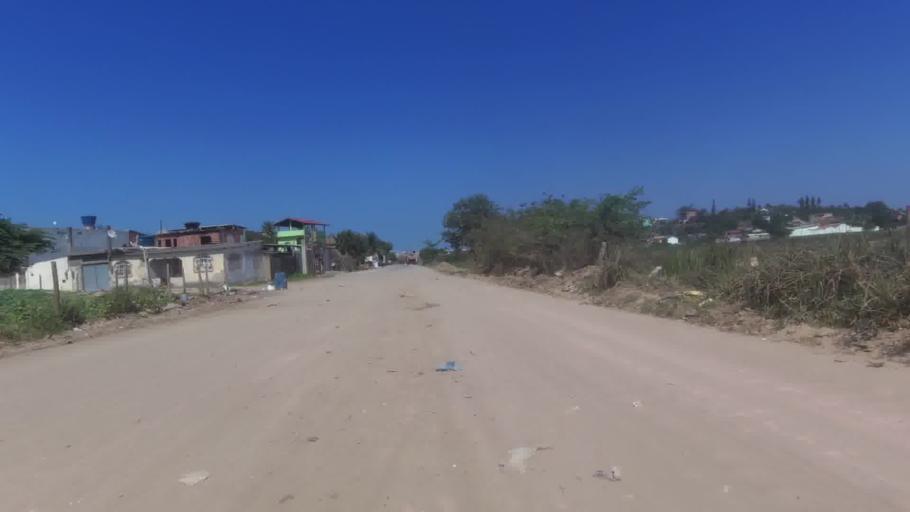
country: BR
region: Espirito Santo
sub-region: Itapemirim
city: Itapemirim
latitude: -21.0140
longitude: -40.8163
